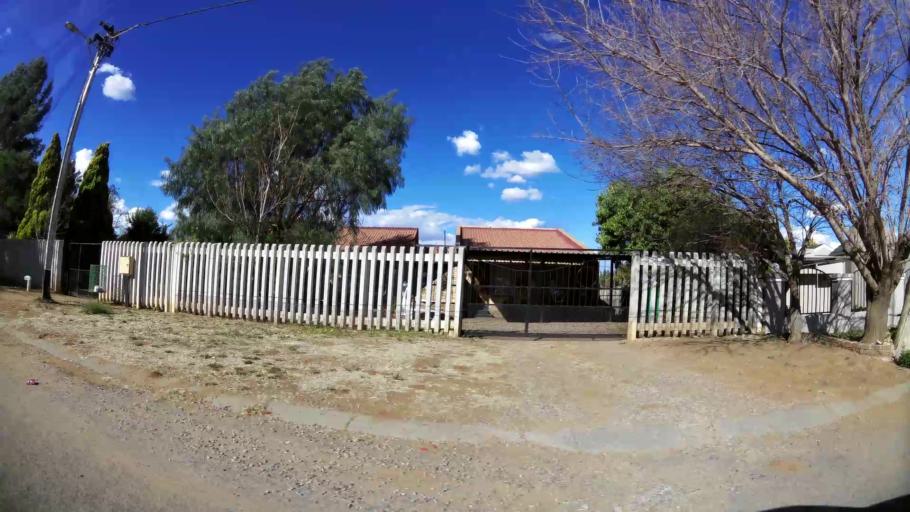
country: ZA
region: North-West
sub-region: Dr Kenneth Kaunda District Municipality
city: Klerksdorp
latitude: -26.8260
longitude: 26.6649
